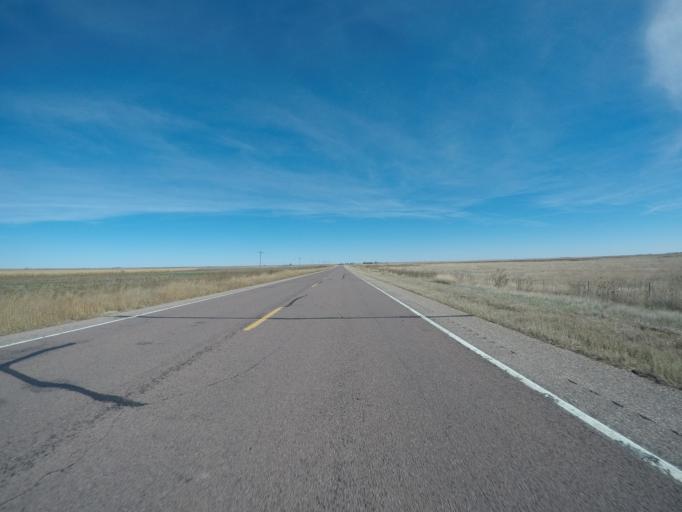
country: US
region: Colorado
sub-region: Kit Carson County
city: Burlington
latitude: 39.6576
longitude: -102.5623
